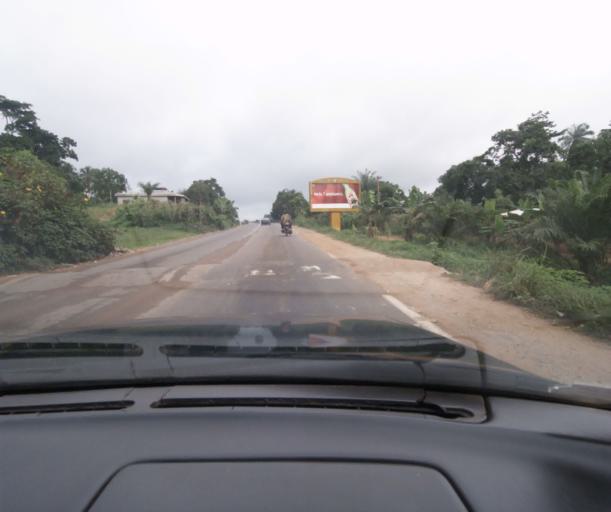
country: CM
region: Centre
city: Obala
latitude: 4.1622
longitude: 11.5038
